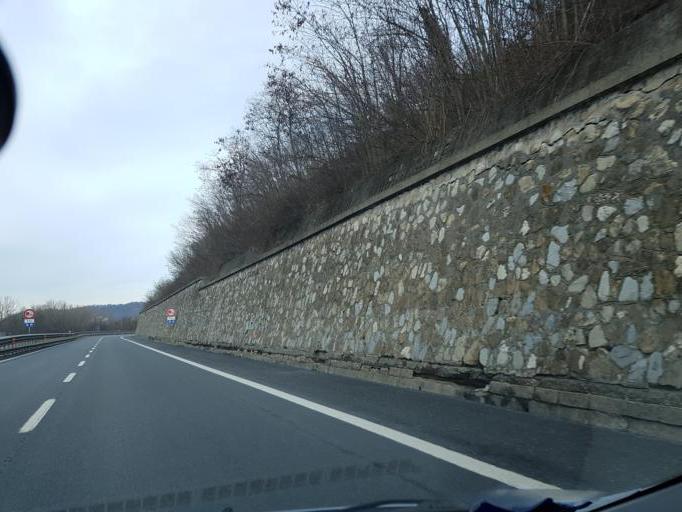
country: IT
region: Piedmont
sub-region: Provincia di Alessandria
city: Arquata Scrivia
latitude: 44.6854
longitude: 8.9027
